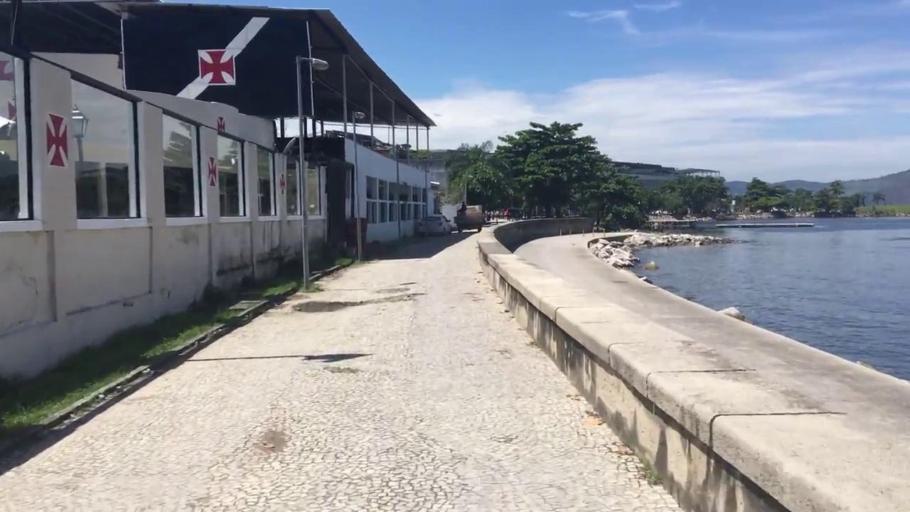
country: BR
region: Rio de Janeiro
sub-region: Rio De Janeiro
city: Rio de Janeiro
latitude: -22.9142
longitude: -43.1694
